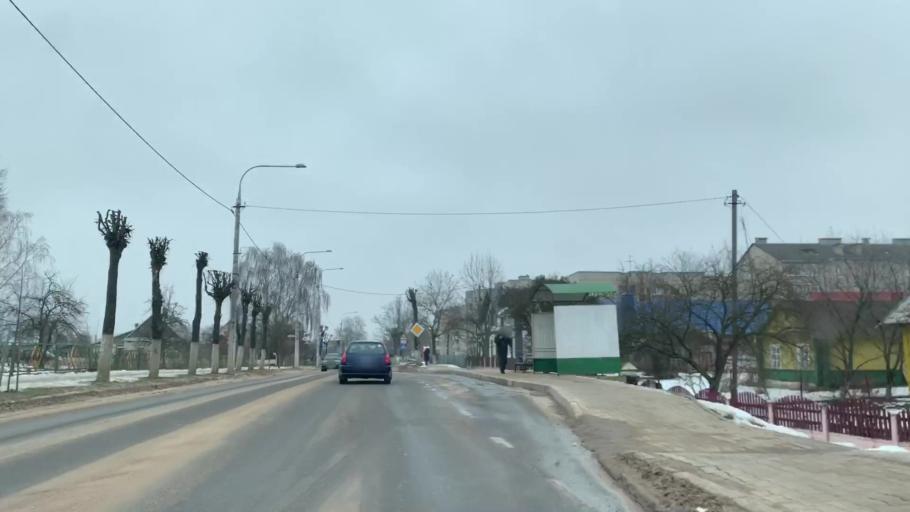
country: BY
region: Minsk
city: Nyasvizh
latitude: 53.2263
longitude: 26.6677
